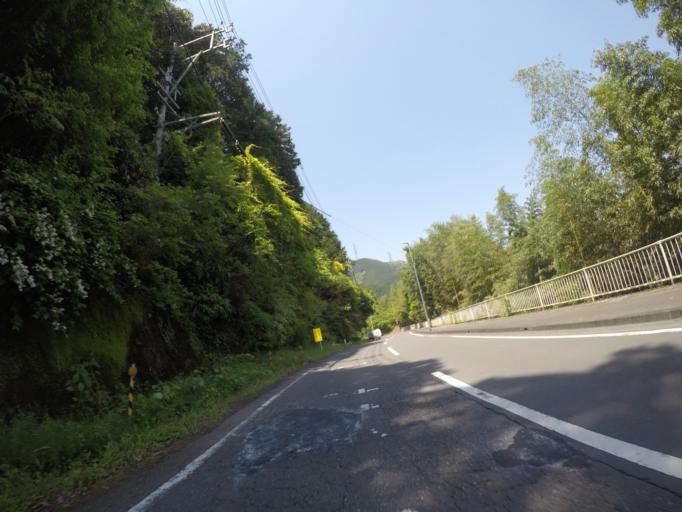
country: JP
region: Shizuoka
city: Shizuoka-shi
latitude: 34.9892
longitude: 138.2920
